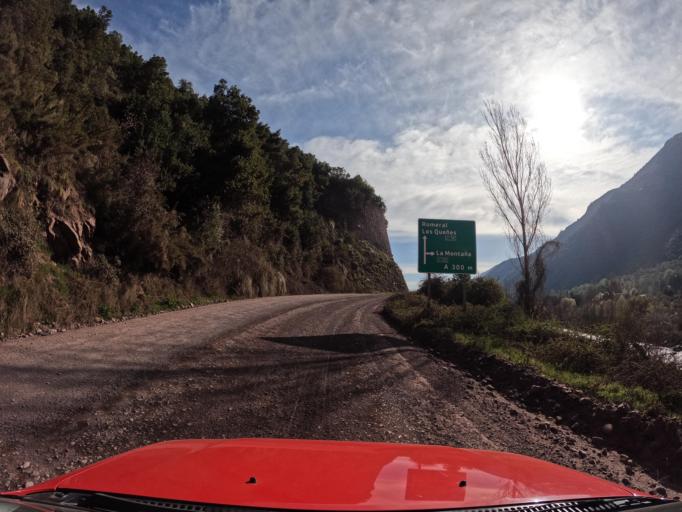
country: CL
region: O'Higgins
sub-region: Provincia de Colchagua
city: Chimbarongo
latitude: -35.0005
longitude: -70.7899
